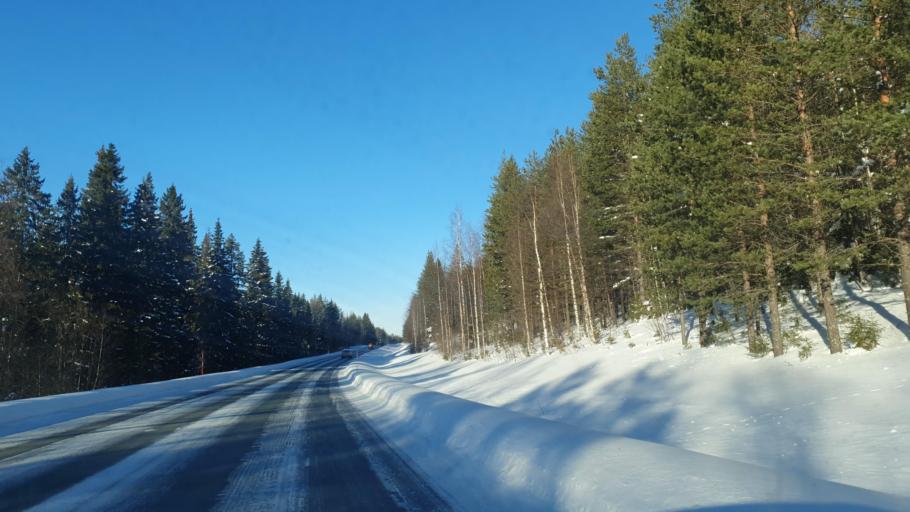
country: FI
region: Lapland
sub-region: Torniolaakso
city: Pello
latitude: 66.6780
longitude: 23.8986
